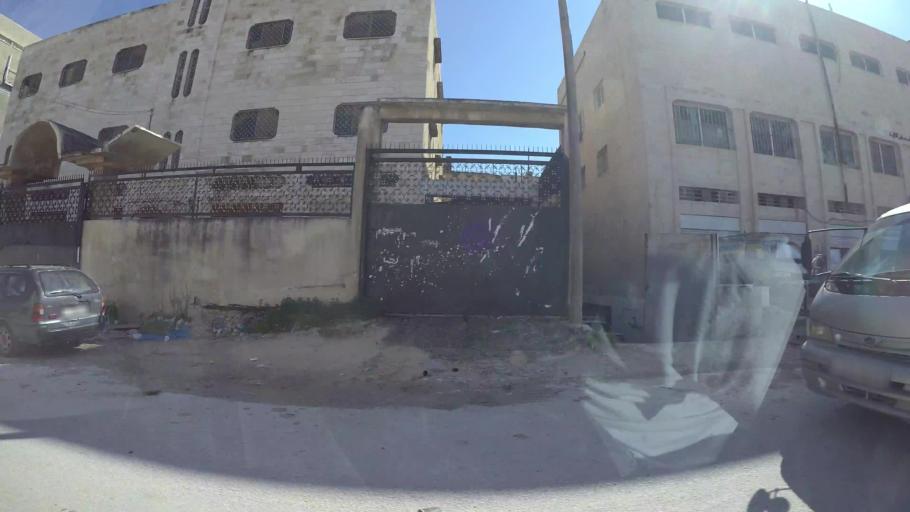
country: JO
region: Amman
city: Al Bunayyat ash Shamaliyah
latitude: 31.9127
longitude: 35.9048
